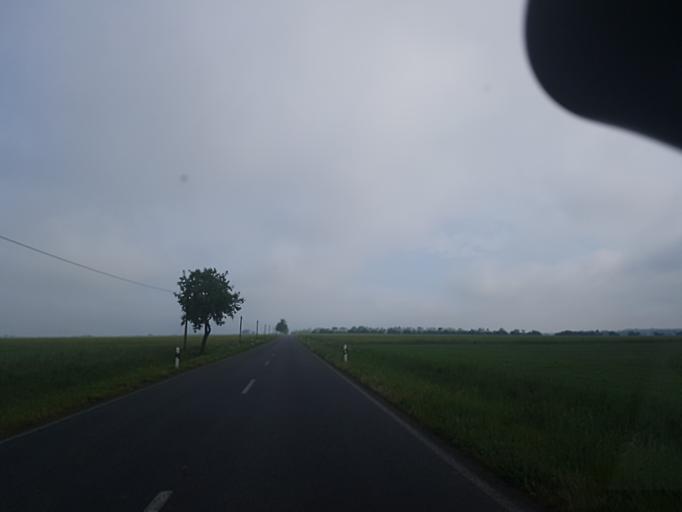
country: DE
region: Saxony-Anhalt
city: Rodleben
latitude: 51.9941
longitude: 12.2313
